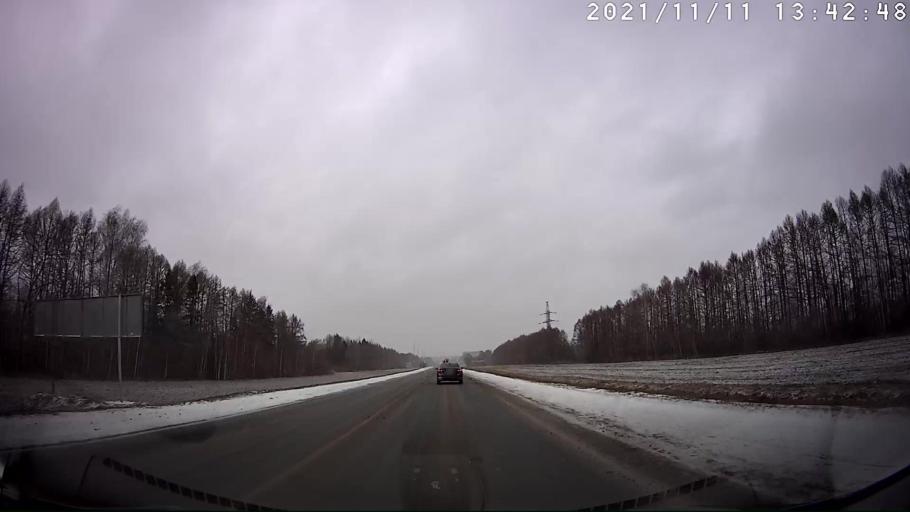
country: RU
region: Chuvashia
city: Kanash
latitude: 55.4797
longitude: 47.4821
